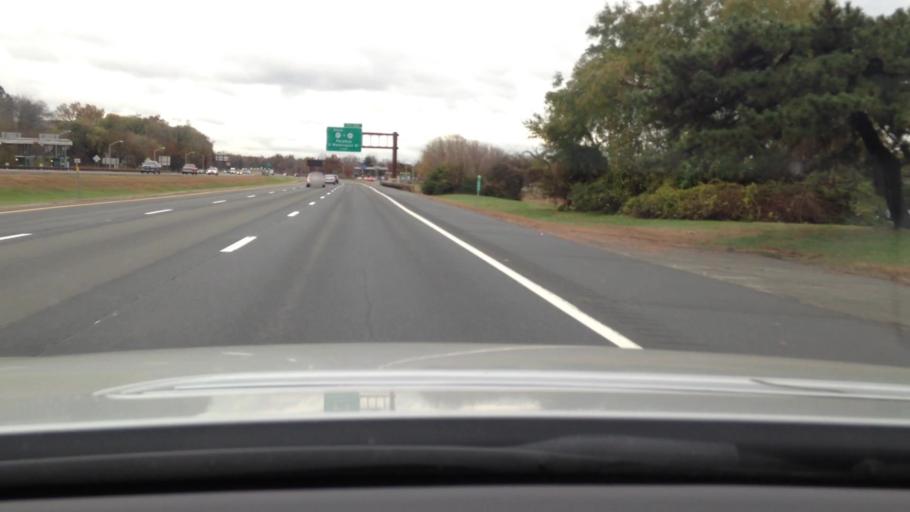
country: US
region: New Jersey
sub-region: Bergen County
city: Paramus
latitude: 40.9613
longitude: -74.0660
